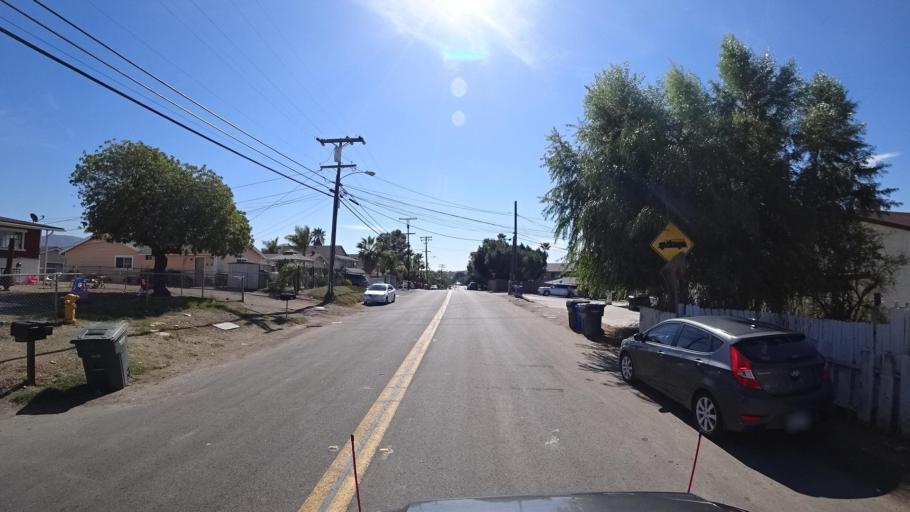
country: US
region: California
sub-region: San Diego County
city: La Presa
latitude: 32.7111
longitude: -117.0075
